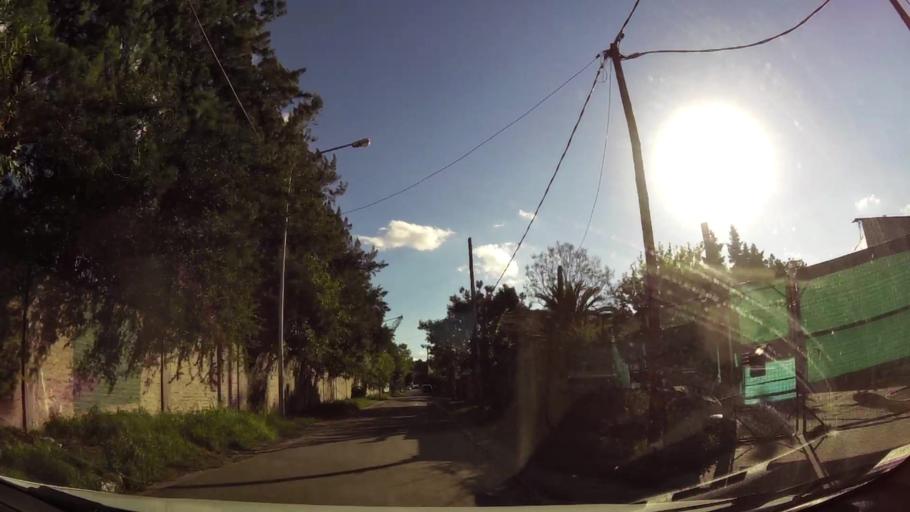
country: AR
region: Buenos Aires
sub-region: Partido de Moron
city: Moron
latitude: -34.6800
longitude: -58.6201
